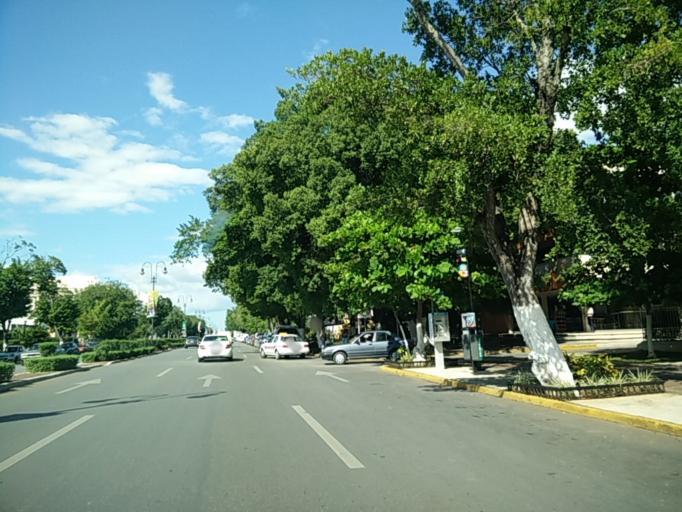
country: MX
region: Yucatan
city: Merida
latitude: 20.9761
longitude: -89.6193
